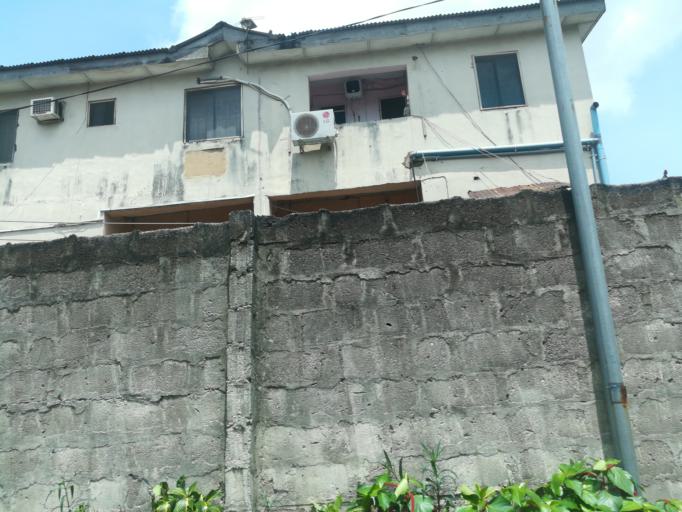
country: NG
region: Lagos
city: Somolu
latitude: 6.5436
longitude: 3.3662
